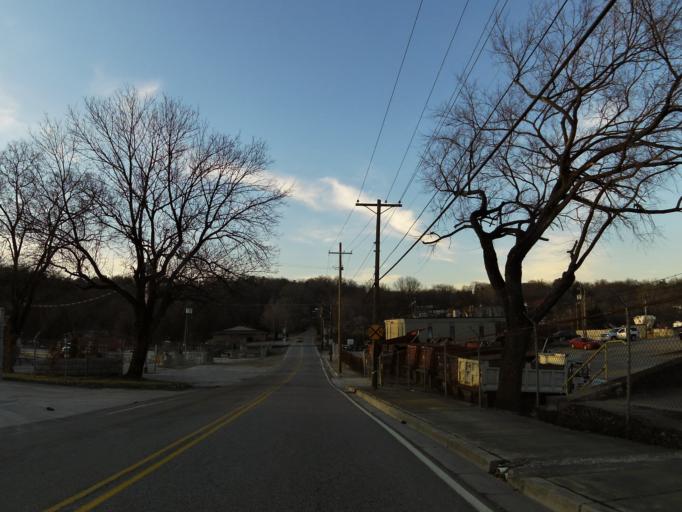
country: US
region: Tennessee
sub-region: Knox County
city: Knoxville
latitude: 36.0132
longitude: -83.8677
